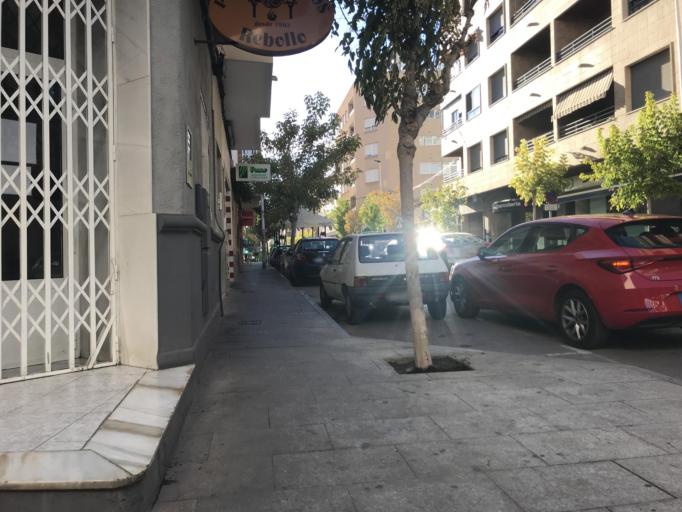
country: ES
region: Valencia
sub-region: Provincia de Alicante
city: Torrevieja
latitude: 37.9807
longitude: -0.6833
